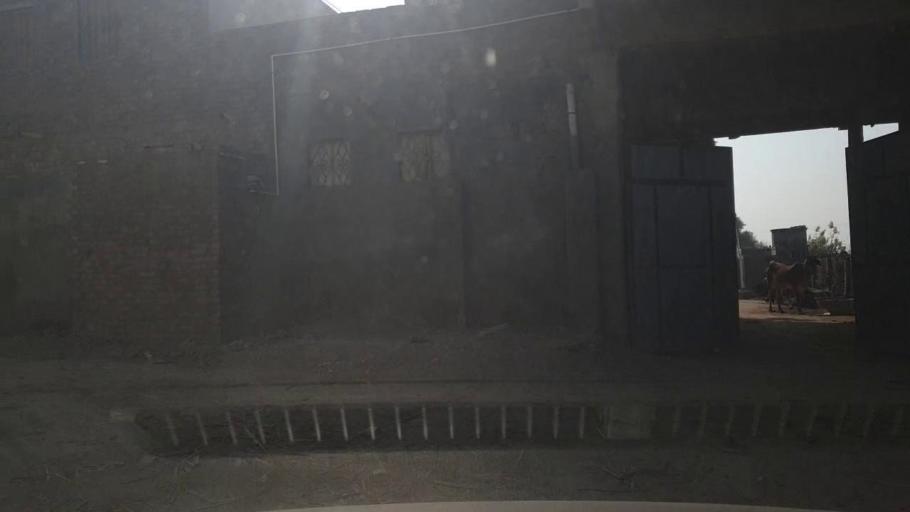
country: PK
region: Sindh
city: Tando Allahyar
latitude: 25.4721
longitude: 68.7515
